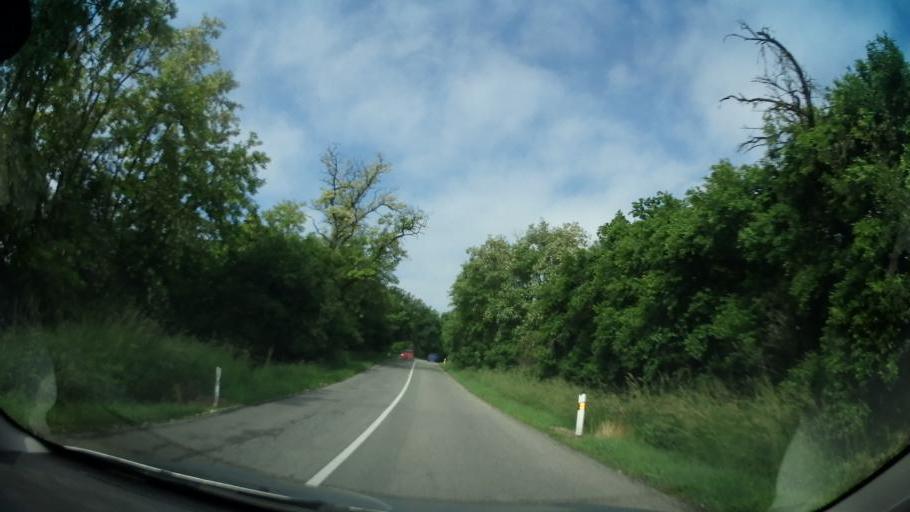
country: CZ
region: South Moravian
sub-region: Okres Brno-Venkov
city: Dolni Loucky
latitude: 49.3707
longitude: 16.3709
